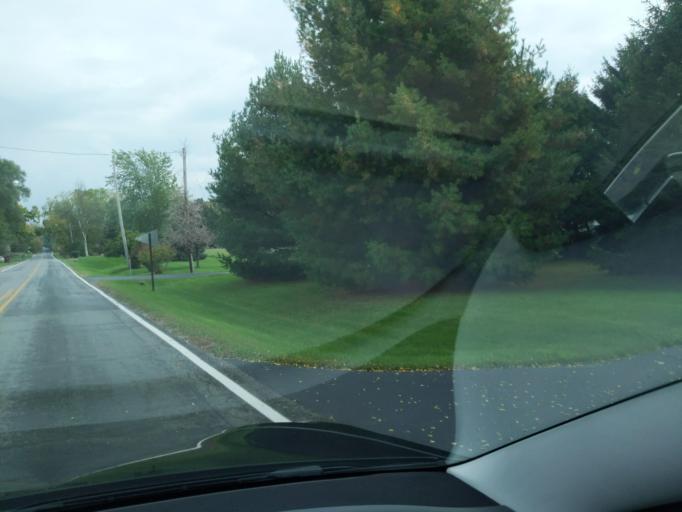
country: US
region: Michigan
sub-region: Eaton County
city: Eaton Rapids
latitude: 42.4656
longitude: -84.5747
